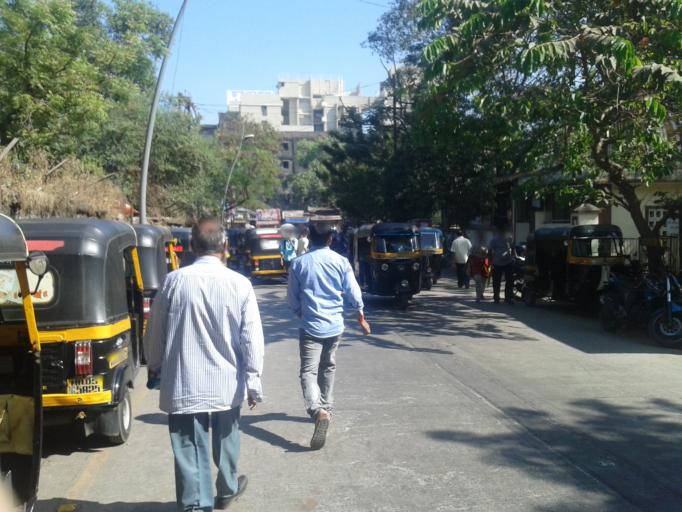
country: IN
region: Maharashtra
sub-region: Thane
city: Dombivli
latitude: 19.2166
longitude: 73.0859
